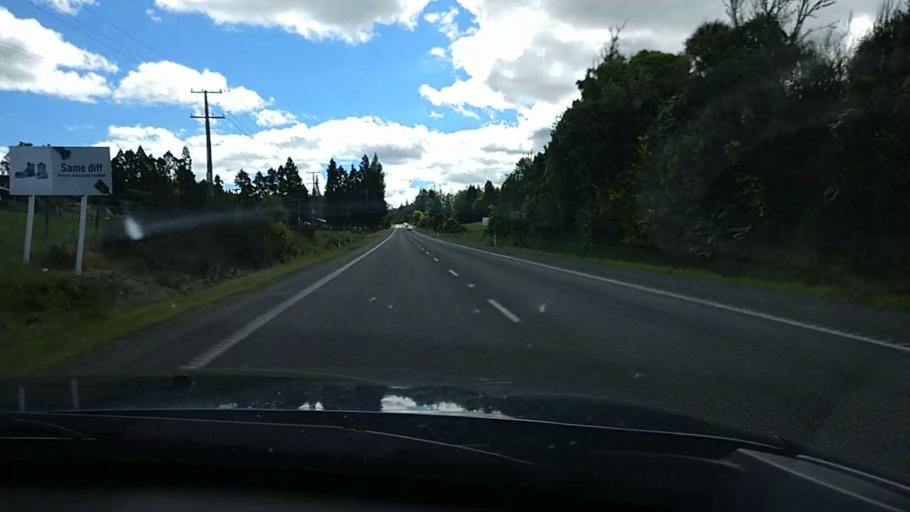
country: NZ
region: Bay of Plenty
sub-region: Rotorua District
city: Rotorua
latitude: -38.0707
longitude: 176.1391
